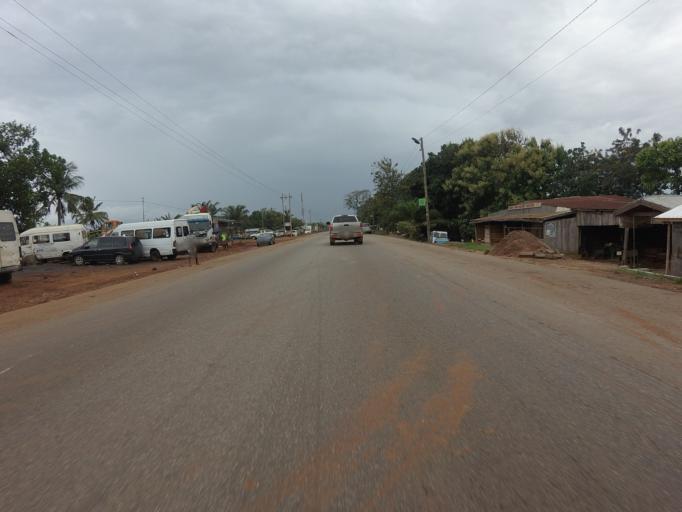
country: GH
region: Ashanti
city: Konongo
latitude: 6.6229
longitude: -1.2010
